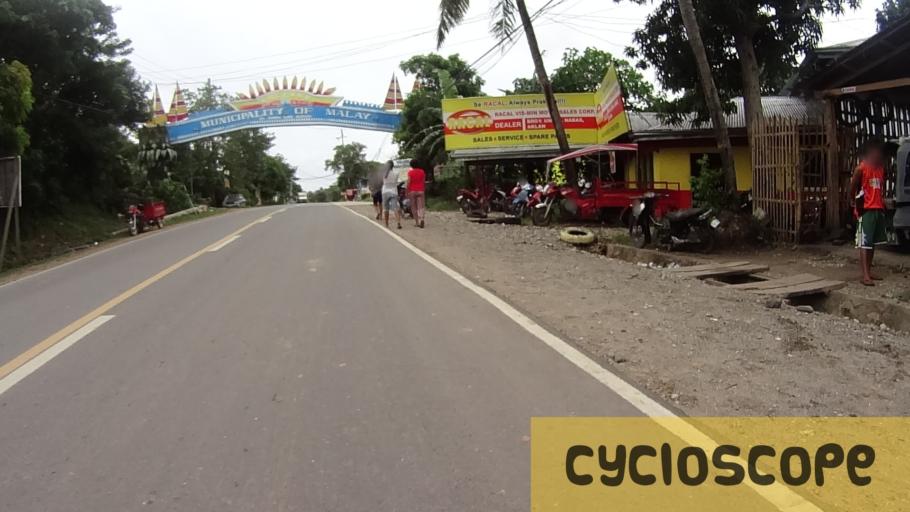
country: PH
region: Western Visayas
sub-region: Province of Aklan
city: Caticlan
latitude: 11.9329
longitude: 121.9582
